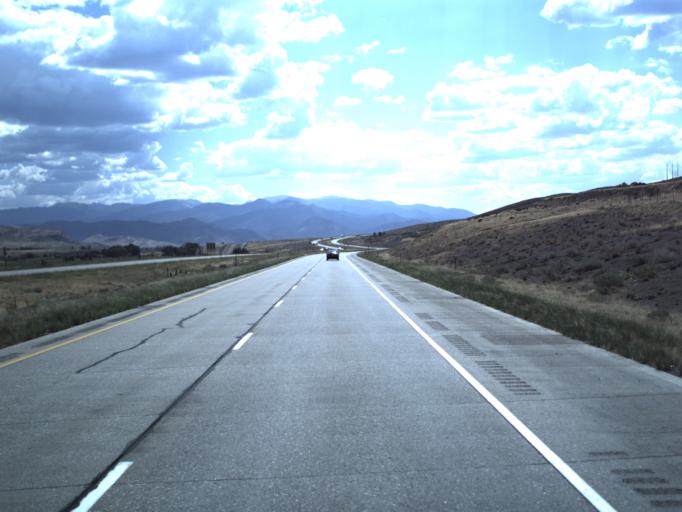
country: US
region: Utah
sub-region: Sevier County
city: Monroe
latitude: 38.6741
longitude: -112.1640
